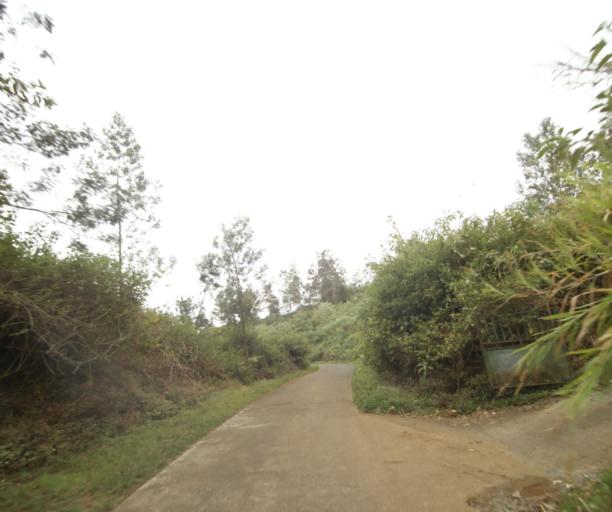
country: RE
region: Reunion
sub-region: Reunion
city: Saint-Paul
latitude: -21.0150
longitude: 55.3504
